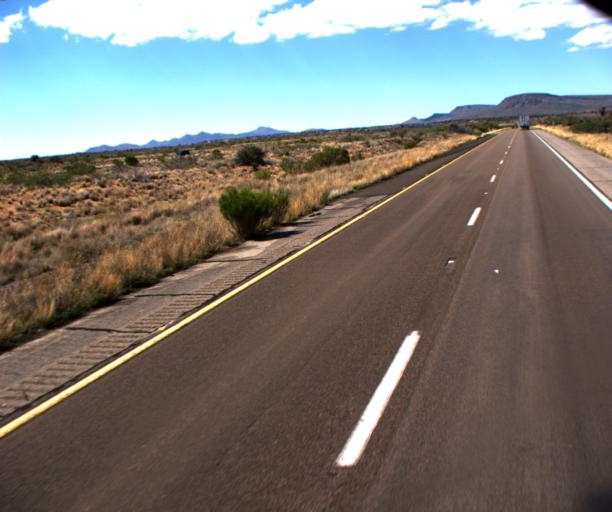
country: US
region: Arizona
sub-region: Mohave County
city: Kingman
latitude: 35.1122
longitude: -113.6660
